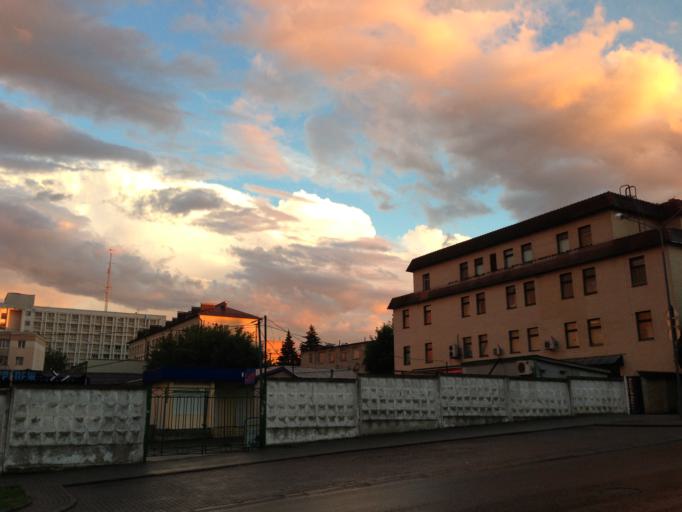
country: BY
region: Grodnenskaya
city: Hrodna
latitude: 53.6938
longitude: 23.8248
